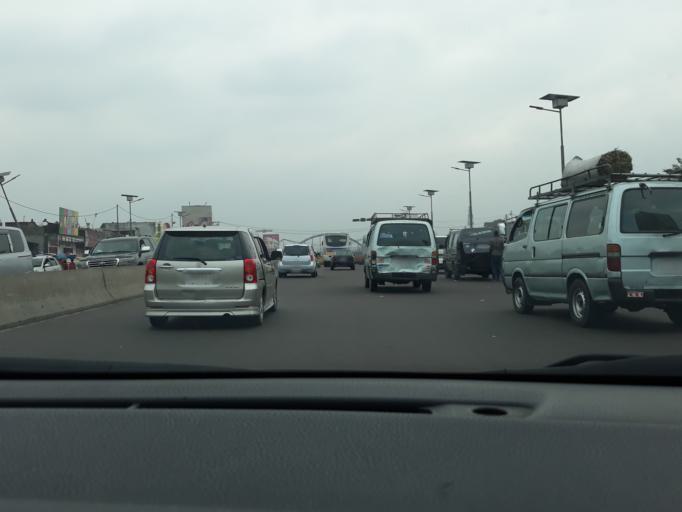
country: CD
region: Kinshasa
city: Masina
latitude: -4.3992
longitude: 15.3979
